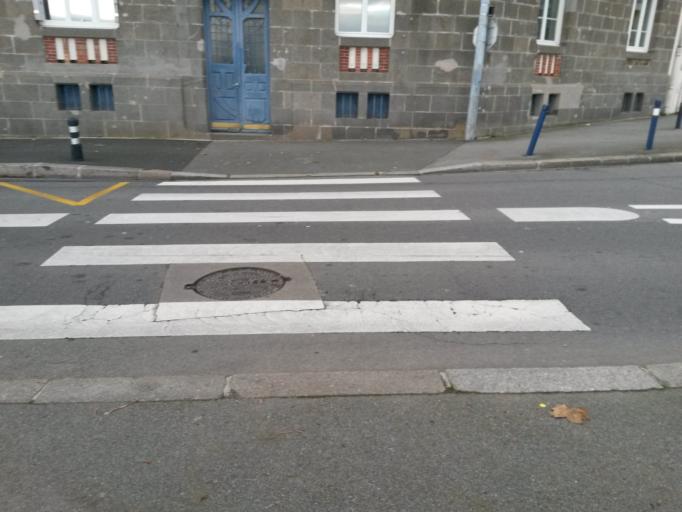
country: FR
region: Brittany
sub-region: Departement du Finistere
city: Brest
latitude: 48.3890
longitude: -4.4788
